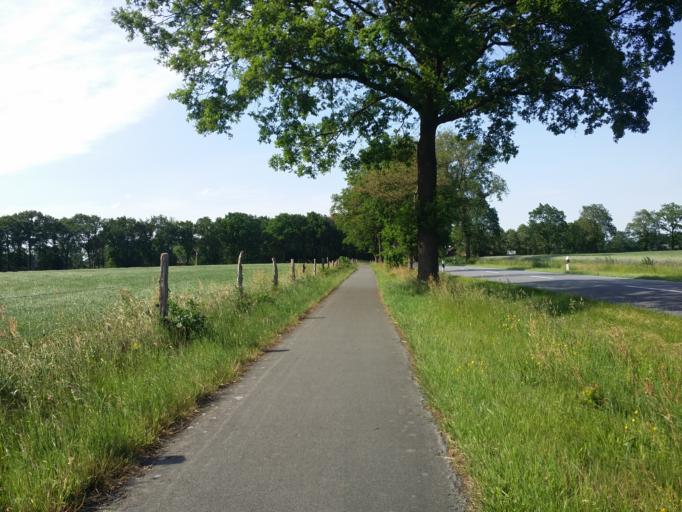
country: DE
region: Lower Saxony
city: Wiefelstede
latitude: 53.2708
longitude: 8.1110
